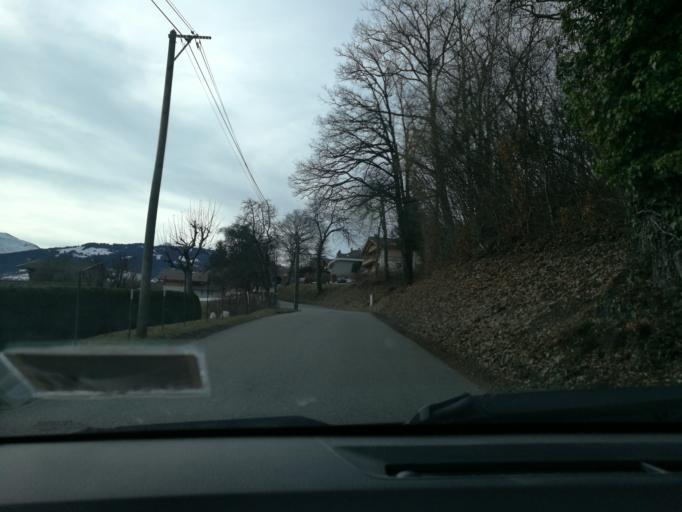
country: FR
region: Rhone-Alpes
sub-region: Departement de la Haute-Savoie
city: Cordon
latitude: 45.9221
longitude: 6.6279
